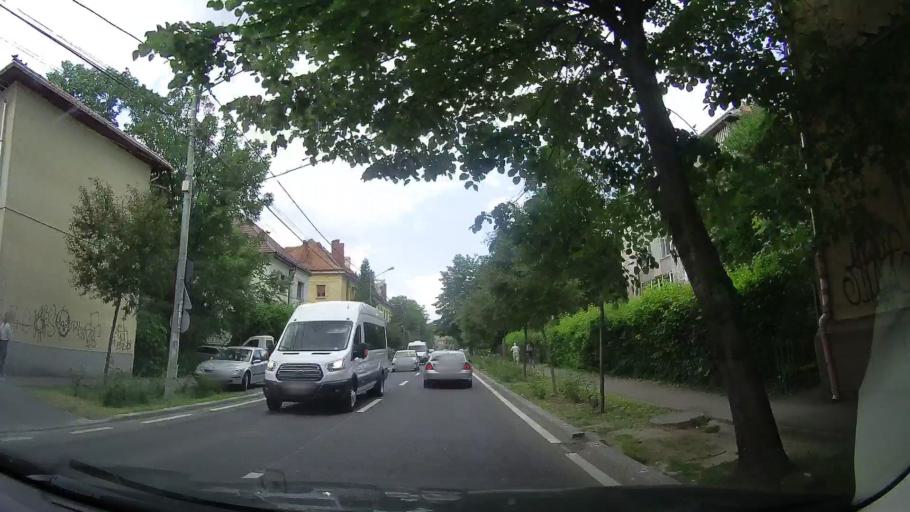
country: RO
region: Timis
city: Timisoara
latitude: 45.7574
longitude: 21.2380
